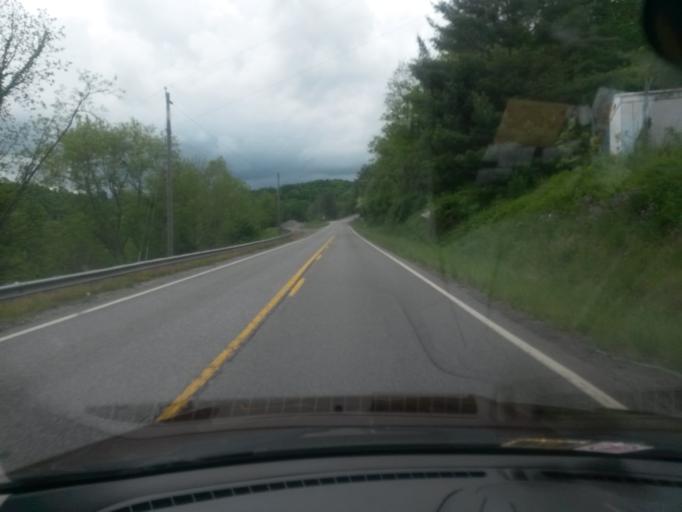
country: US
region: Virginia
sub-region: Floyd County
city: Floyd
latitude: 36.9399
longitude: -80.3446
